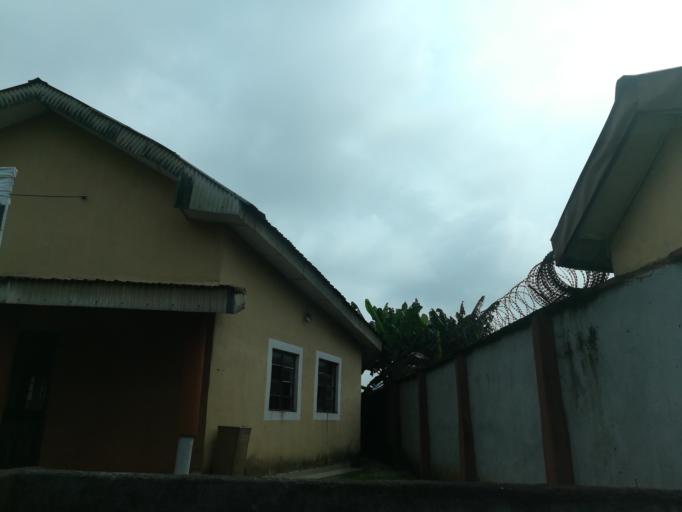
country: NG
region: Rivers
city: Port Harcourt
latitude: 4.8722
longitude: 6.9832
